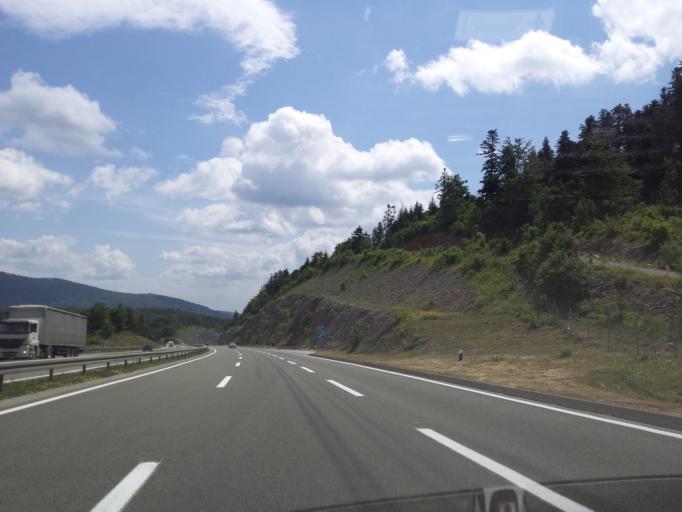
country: HR
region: Primorsko-Goranska
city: Vrbovsko
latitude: 45.3762
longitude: 15.0392
